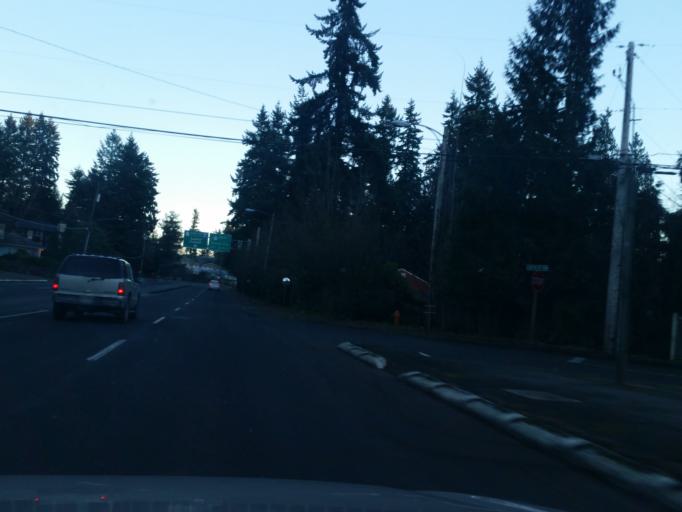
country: US
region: Washington
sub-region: Snohomish County
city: Esperance
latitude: 47.7834
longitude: -122.3521
